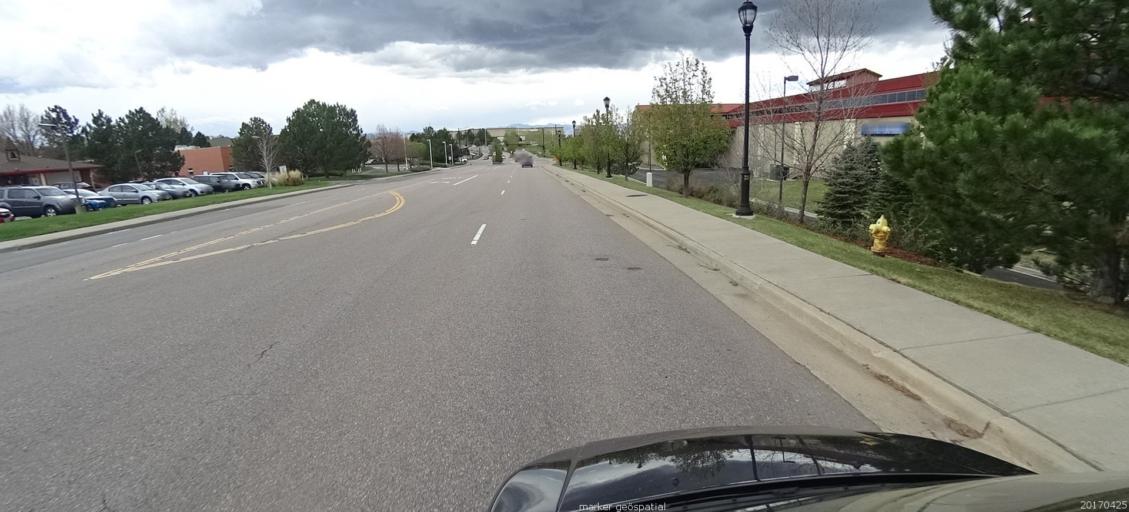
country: US
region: Colorado
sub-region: Douglas County
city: Acres Green
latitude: 39.5631
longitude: -104.8944
